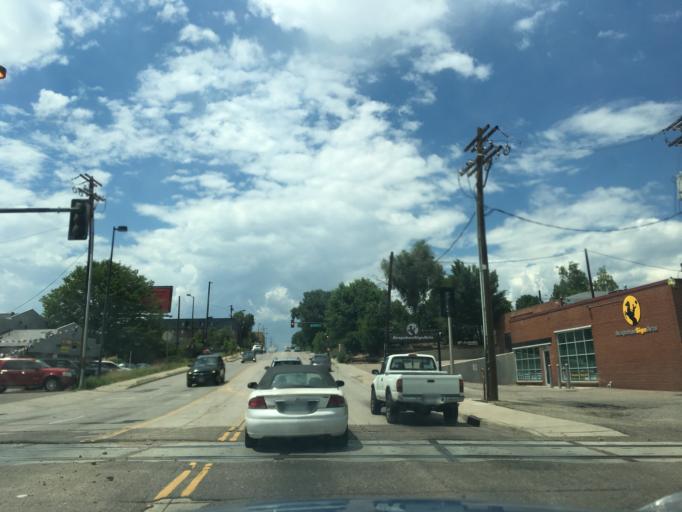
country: US
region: Colorado
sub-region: Denver County
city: Denver
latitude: 39.6967
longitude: -105.0004
